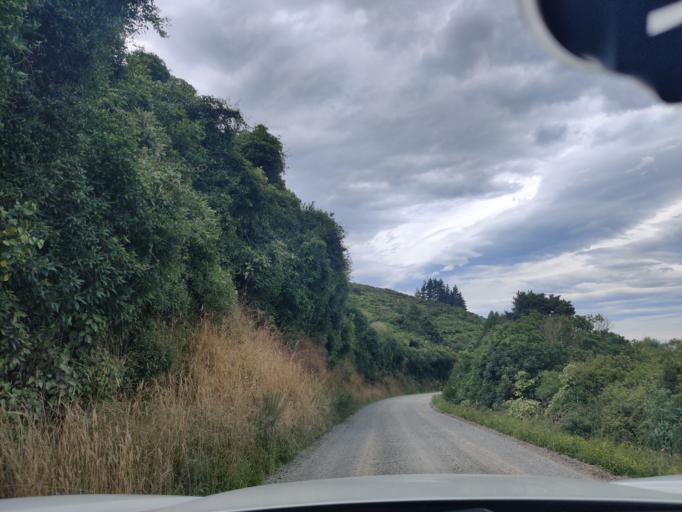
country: NZ
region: Wellington
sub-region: Masterton District
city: Masterton
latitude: -41.0400
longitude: 175.4111
